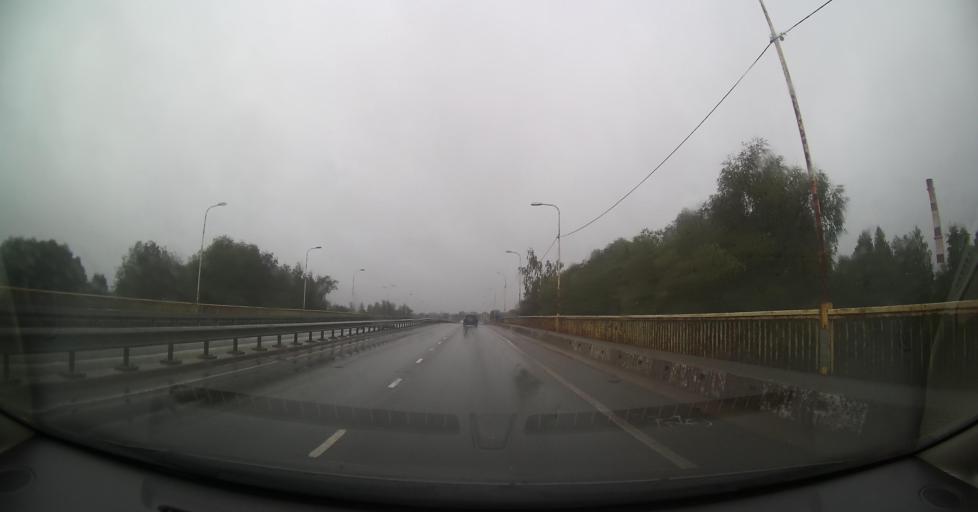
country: EE
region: Tartu
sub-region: Tartu linn
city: Tartu
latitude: 58.3727
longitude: 26.7439
